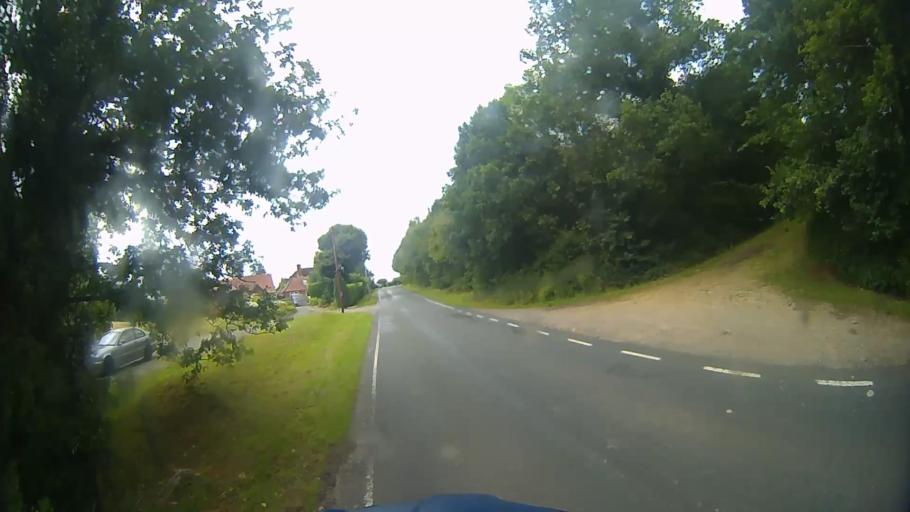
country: GB
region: England
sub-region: Hampshire
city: Kingsley
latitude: 51.1569
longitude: -0.8518
